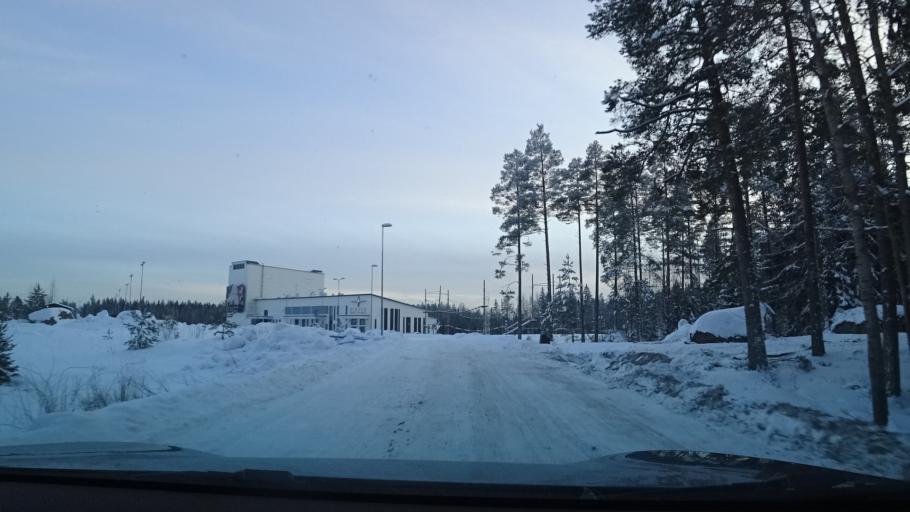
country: FI
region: Kymenlaakso
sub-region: Kotka-Hamina
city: Pyhtaeae
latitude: 60.4897
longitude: 26.5545
